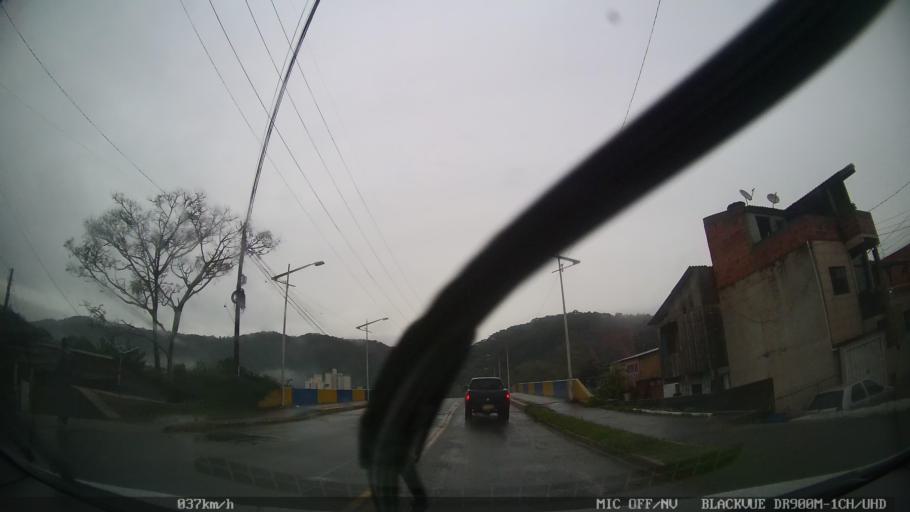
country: BR
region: Santa Catarina
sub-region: Itajai
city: Itajai
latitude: -26.9314
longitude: -48.6913
